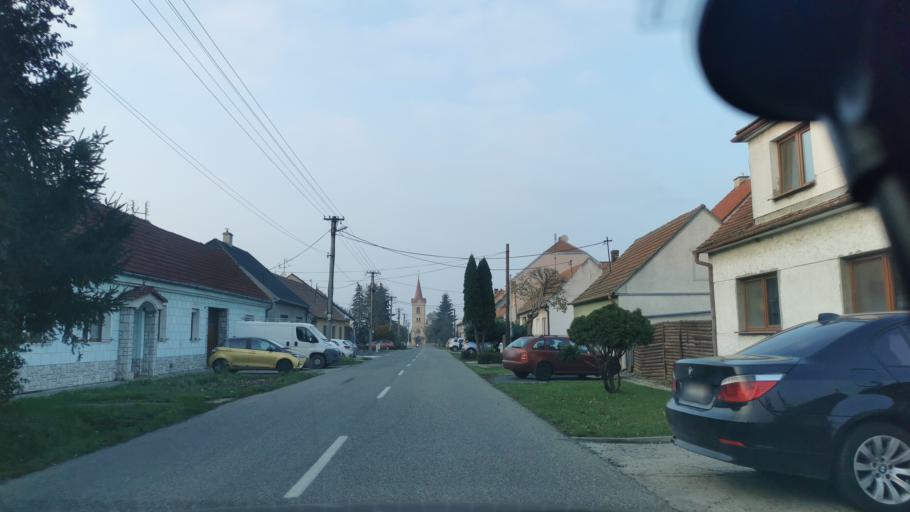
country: SK
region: Trnavsky
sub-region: Okres Skalica
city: Holic
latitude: 48.8221
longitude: 17.1928
